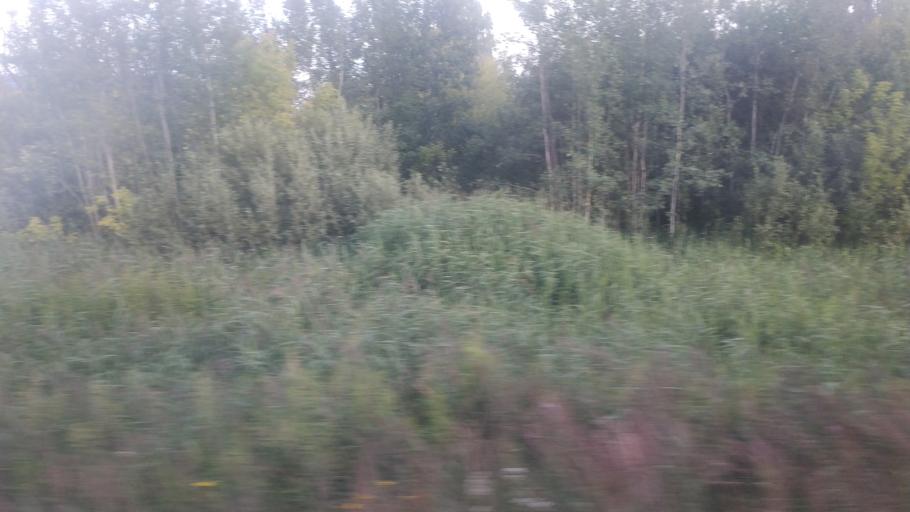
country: RU
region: Moskovskaya
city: Tugolesskiy Bor
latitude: 55.5534
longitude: 39.6970
